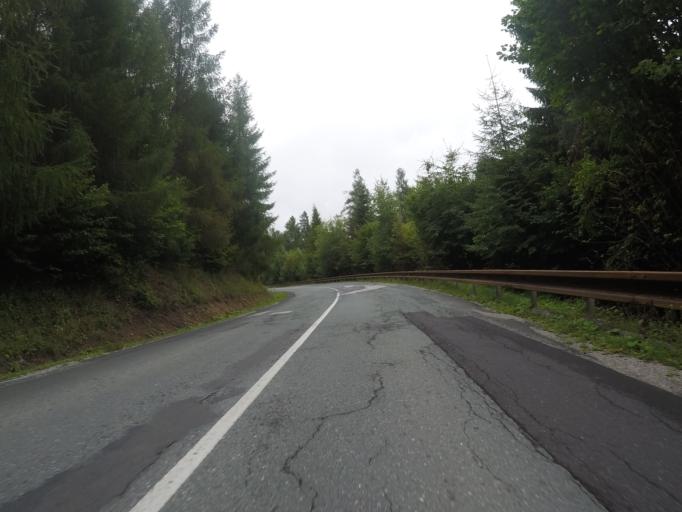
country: SK
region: Kosicky
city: Spisska Nova Ves
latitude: 48.8904
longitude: 20.5341
